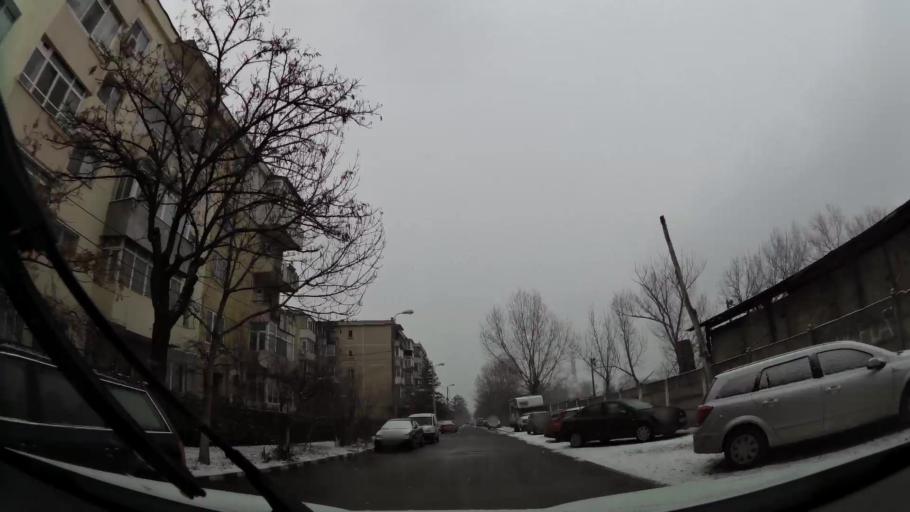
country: RO
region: Prahova
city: Ploiesti
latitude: 44.9353
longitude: 25.9991
